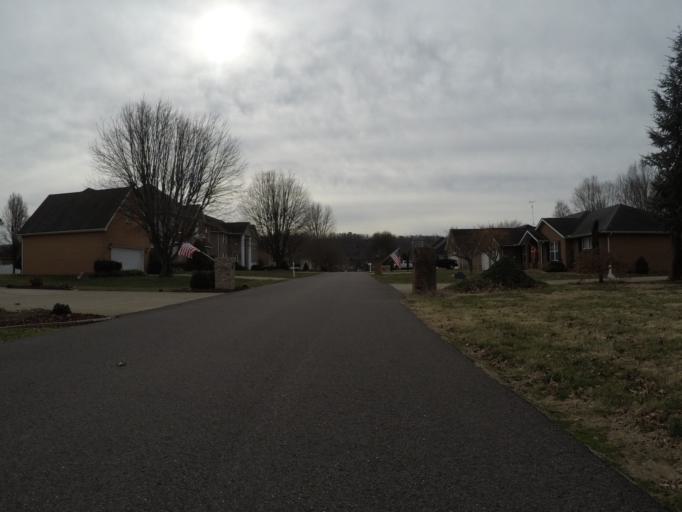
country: US
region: West Virginia
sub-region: Cabell County
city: Pea Ridge
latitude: 38.4443
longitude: -82.3498
